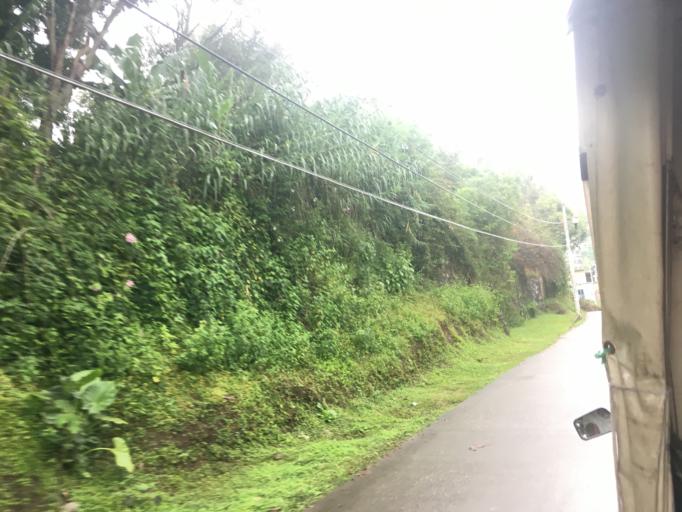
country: MX
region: Morelos
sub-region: Tlayacapan
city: Tlayacapan
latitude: 18.9544
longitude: -98.9882
